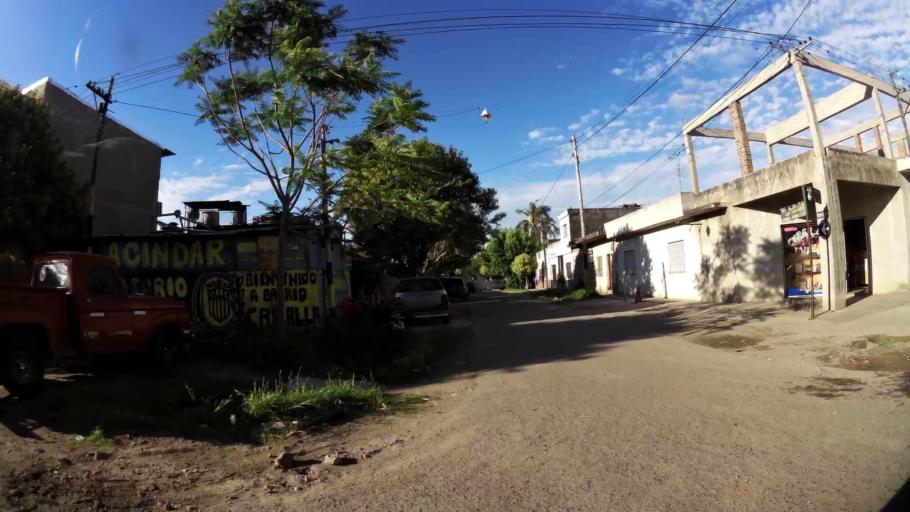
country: AR
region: Santa Fe
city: Gobernador Galvez
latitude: -32.9881
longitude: -60.6766
